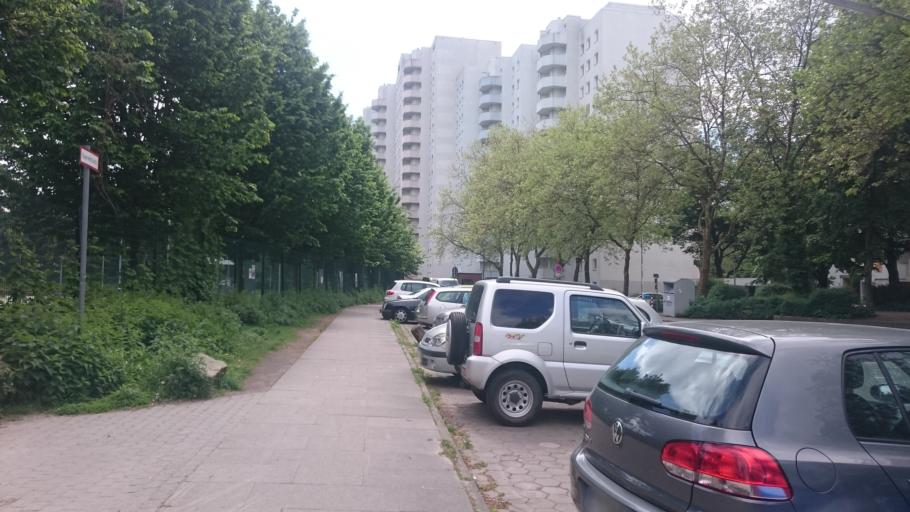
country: DE
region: Hamburg
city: Stellingen
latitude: 53.5846
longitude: 9.9503
